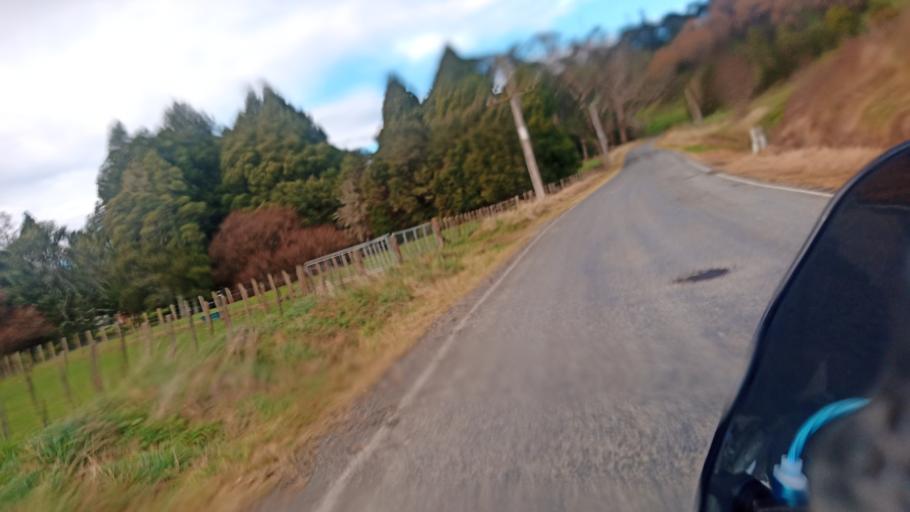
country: NZ
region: Gisborne
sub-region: Gisborne District
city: Gisborne
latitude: -38.4083
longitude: 177.9394
